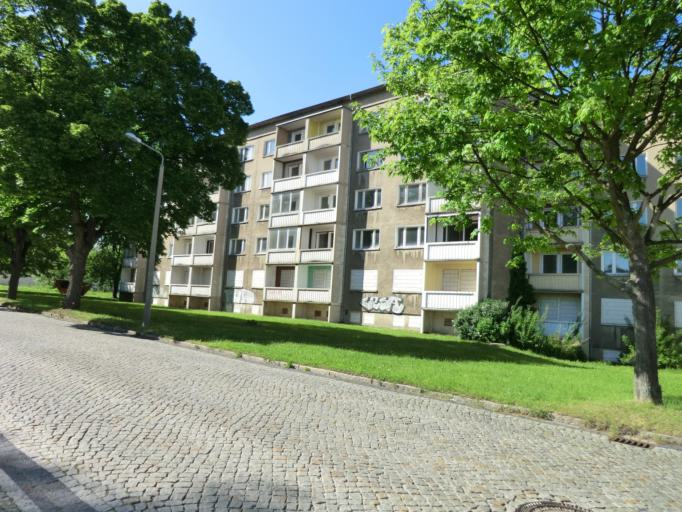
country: DE
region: Saxony
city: Goerlitz
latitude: 51.1275
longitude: 14.9763
